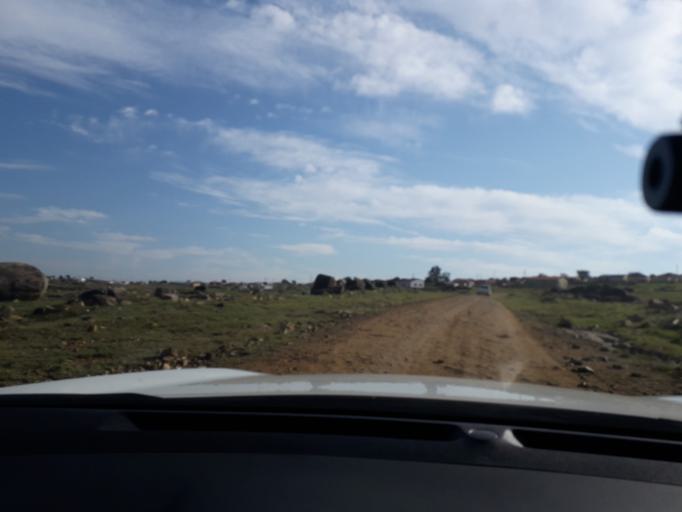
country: ZA
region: Eastern Cape
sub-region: Buffalo City Metropolitan Municipality
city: Bhisho
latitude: -32.9425
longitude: 27.2893
